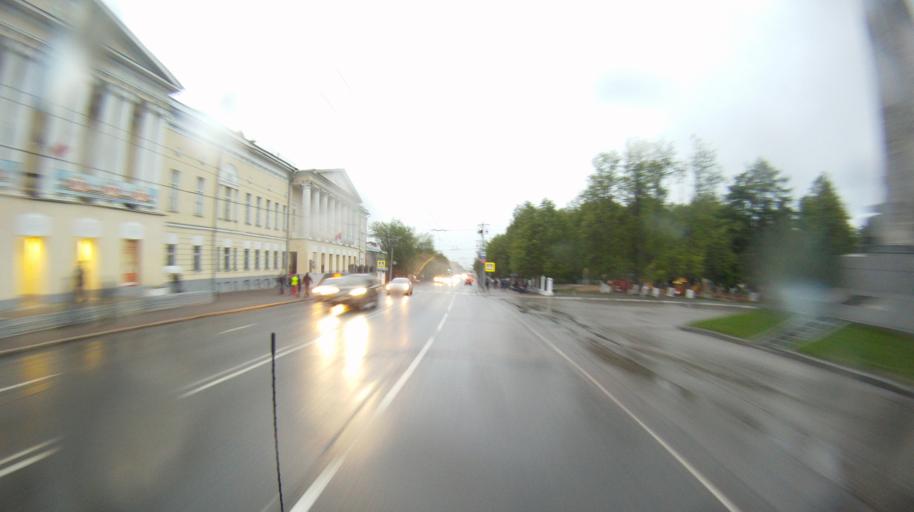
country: RU
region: Vladimir
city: Vladimir
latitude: 56.1290
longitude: 40.4074
